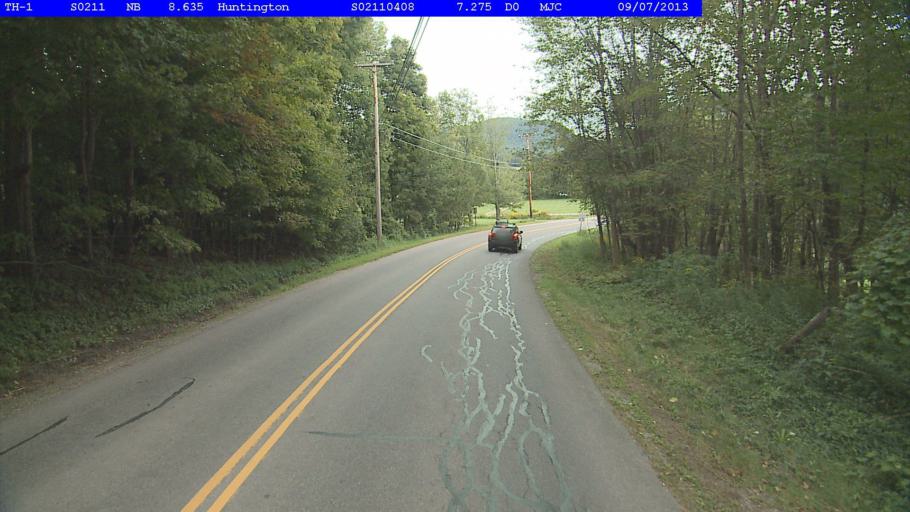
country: US
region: Vermont
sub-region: Chittenden County
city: Hinesburg
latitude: 44.3235
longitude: -72.9884
